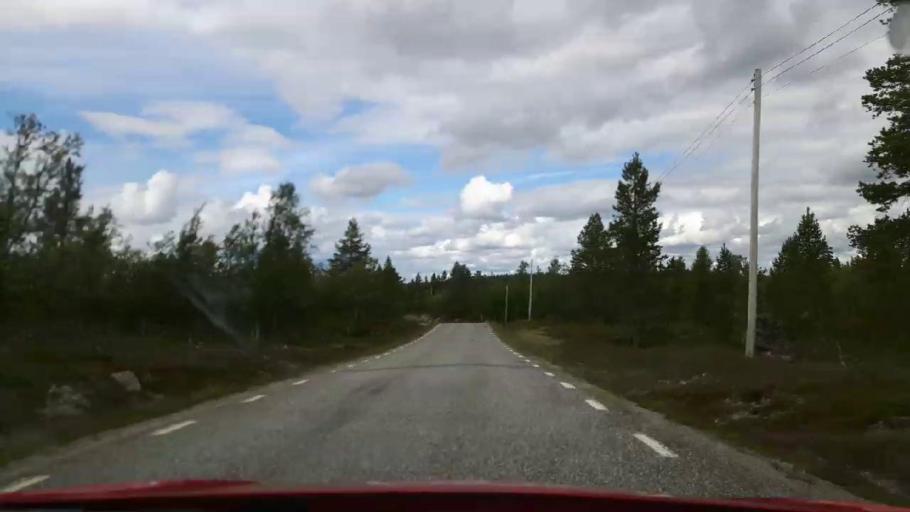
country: NO
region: Hedmark
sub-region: Engerdal
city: Engerdal
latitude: 62.3440
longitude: 12.7973
